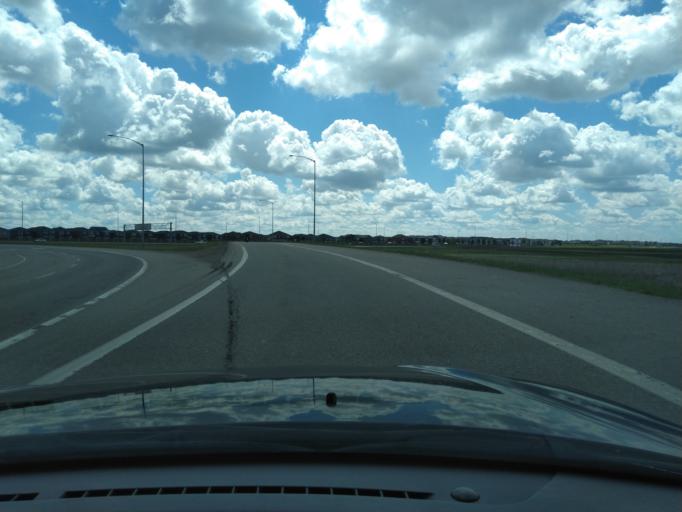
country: CA
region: Alberta
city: Airdrie
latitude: 51.1737
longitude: -113.9722
